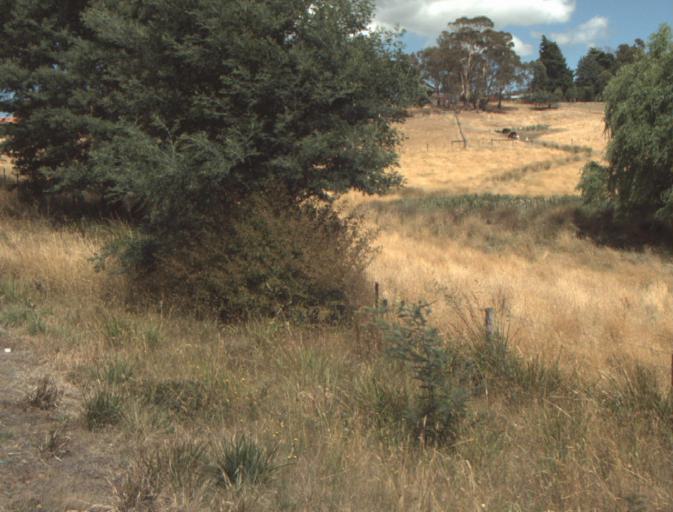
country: AU
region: Tasmania
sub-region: Launceston
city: Mayfield
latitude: -41.2155
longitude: 147.1404
